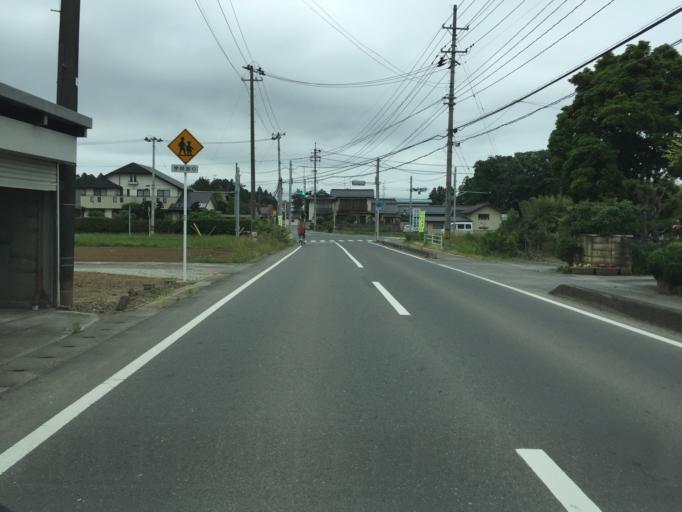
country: JP
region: Miyagi
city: Marumori
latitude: 37.7747
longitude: 140.9125
